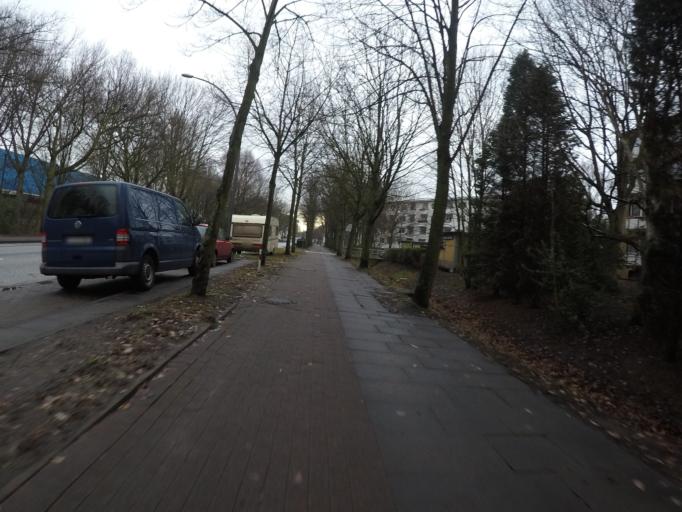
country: DE
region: Hamburg
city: Harburg
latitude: 53.4914
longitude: 9.9904
